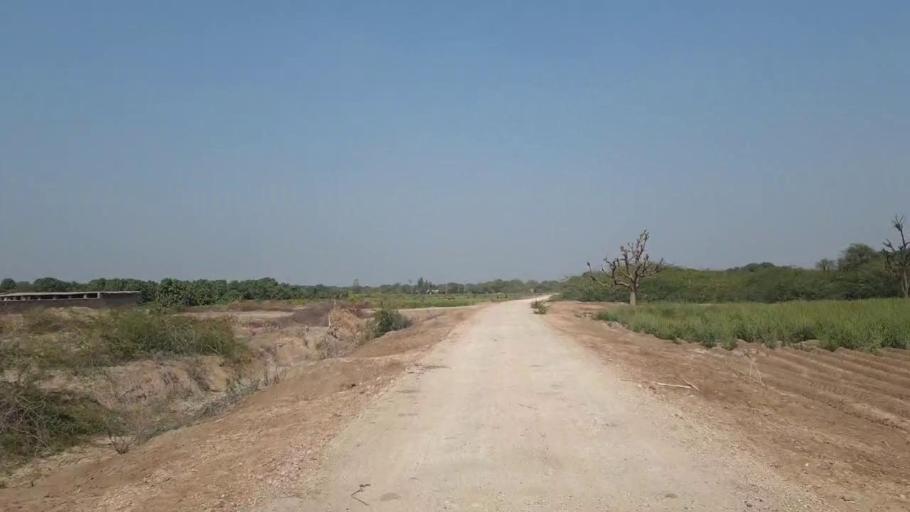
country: PK
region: Sindh
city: Chambar
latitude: 25.4005
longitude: 68.9019
